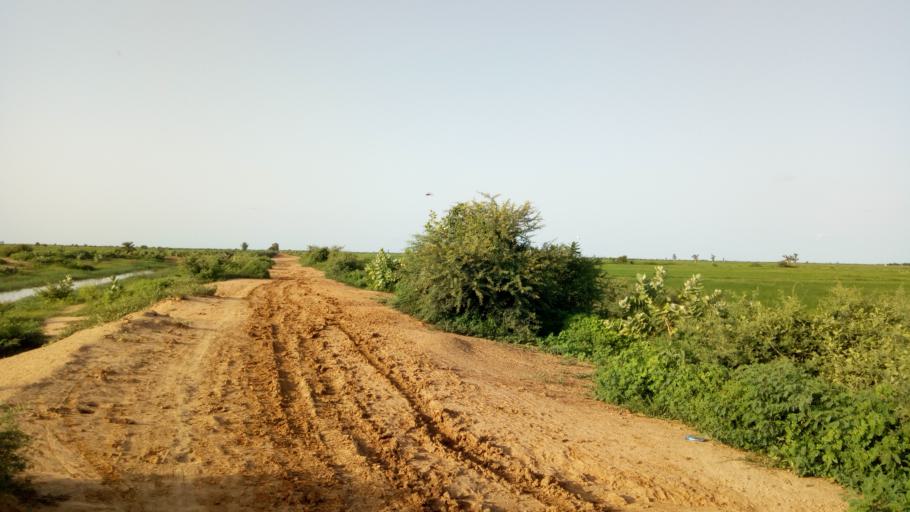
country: ML
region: Segou
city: Niono
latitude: 14.3034
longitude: -5.9403
